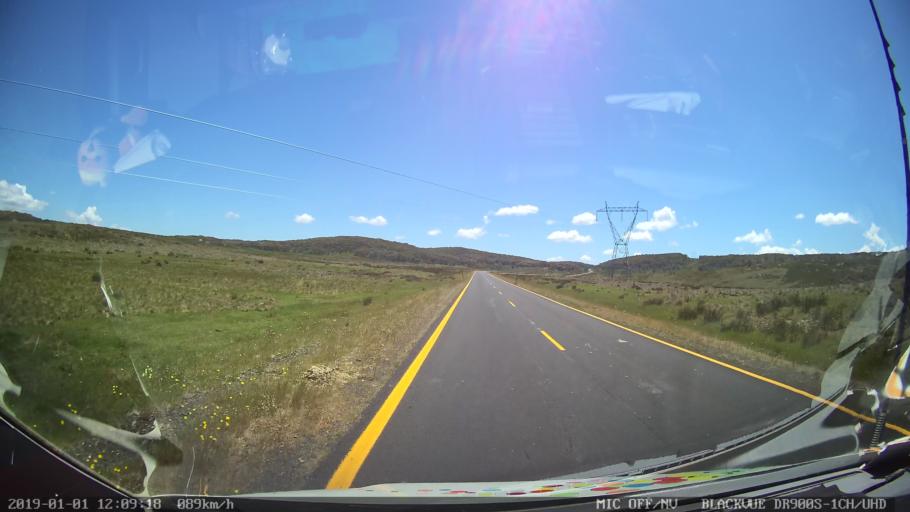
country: AU
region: New South Wales
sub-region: Tumut Shire
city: Tumut
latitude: -35.8090
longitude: 148.4961
